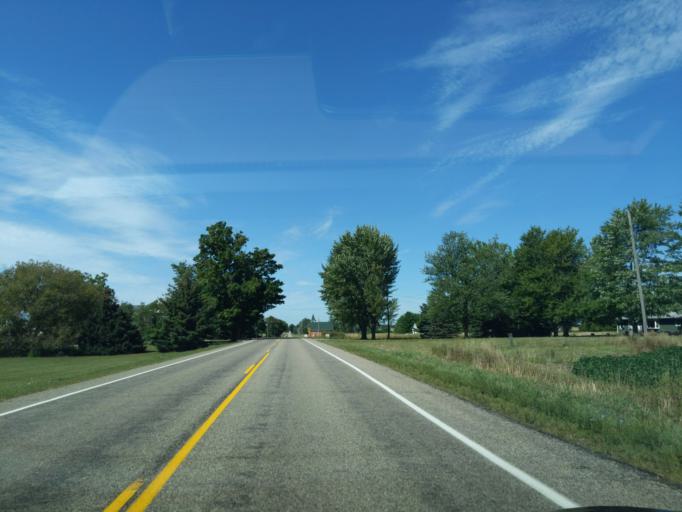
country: US
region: Michigan
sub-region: Eaton County
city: Charlotte
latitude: 42.6260
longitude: -84.8129
